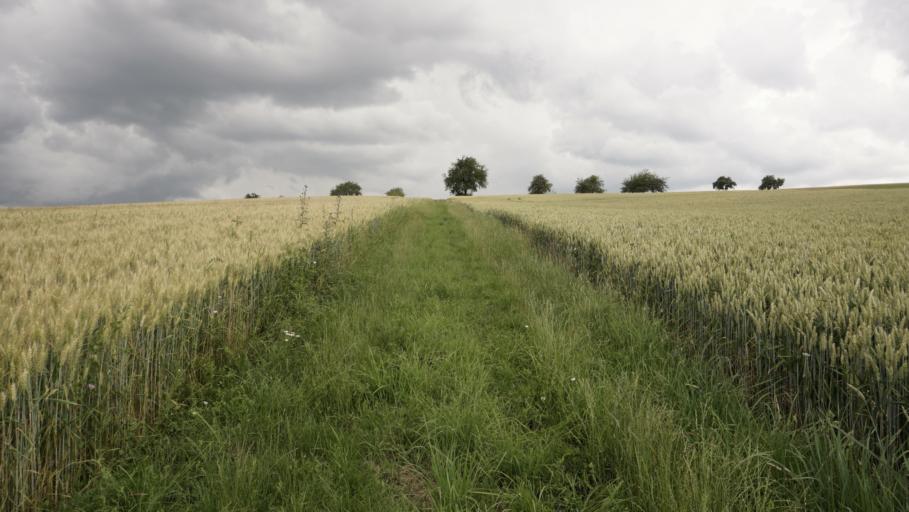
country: DE
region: Baden-Wuerttemberg
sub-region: Karlsruhe Region
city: Mosbach
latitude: 49.3648
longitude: 9.1836
